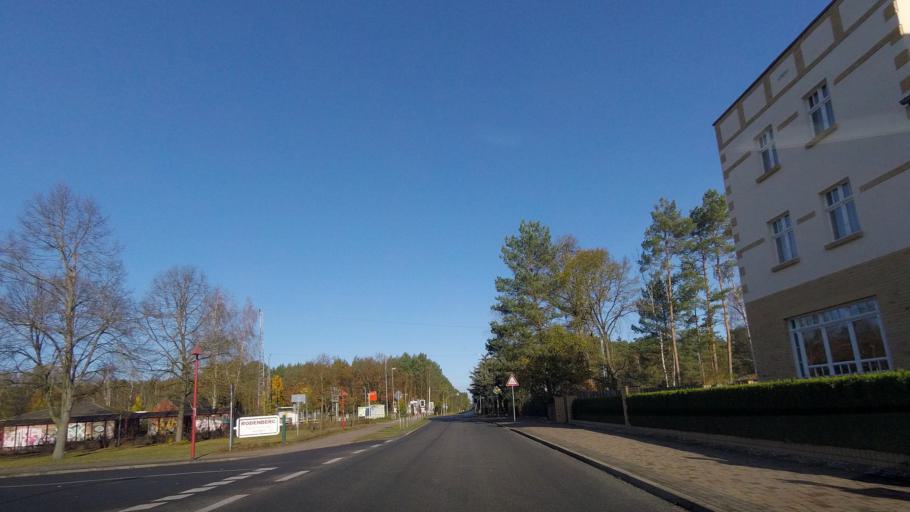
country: DE
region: Brandenburg
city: Borkheide
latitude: 52.2304
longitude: 12.8556
